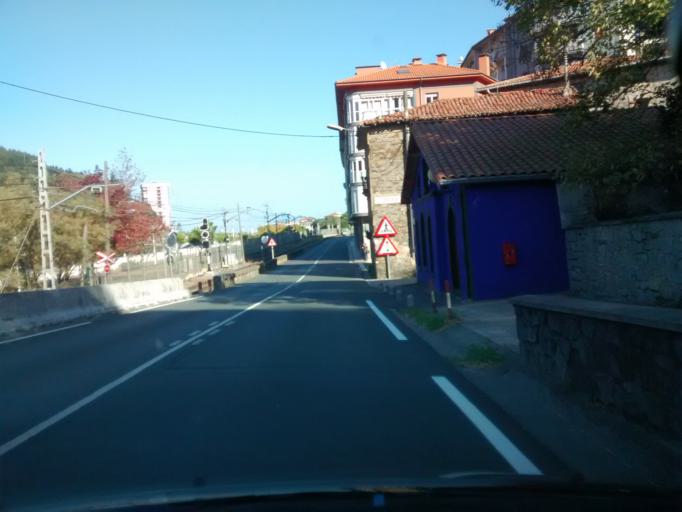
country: ES
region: Basque Country
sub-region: Provincia de Guipuzcoa
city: Deba
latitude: 43.2904
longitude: -2.3570
